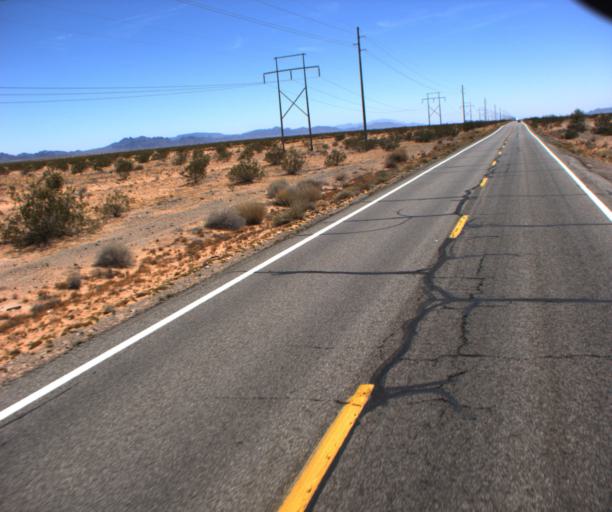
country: US
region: Arizona
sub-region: La Paz County
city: Quartzsite
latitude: 33.8907
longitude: -114.2169
